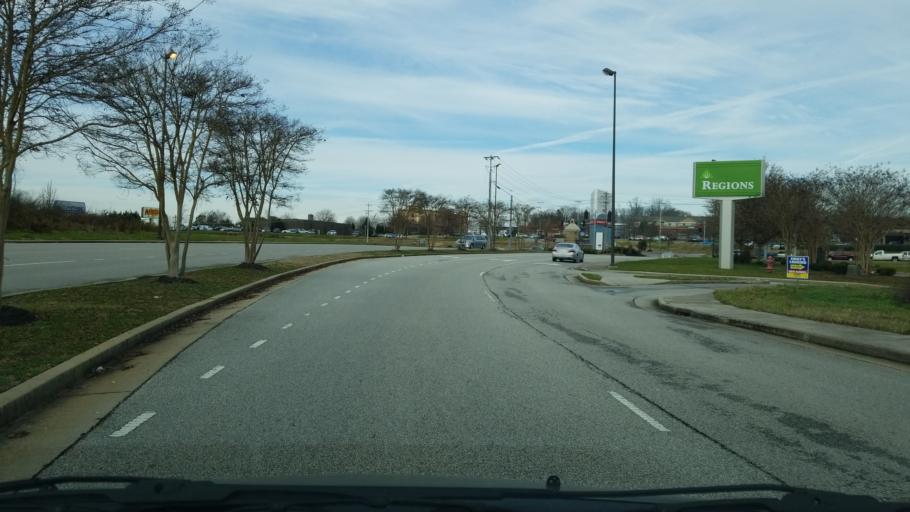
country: US
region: Tennessee
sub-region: Loudon County
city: Lenoir City
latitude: 35.8222
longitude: -84.2719
